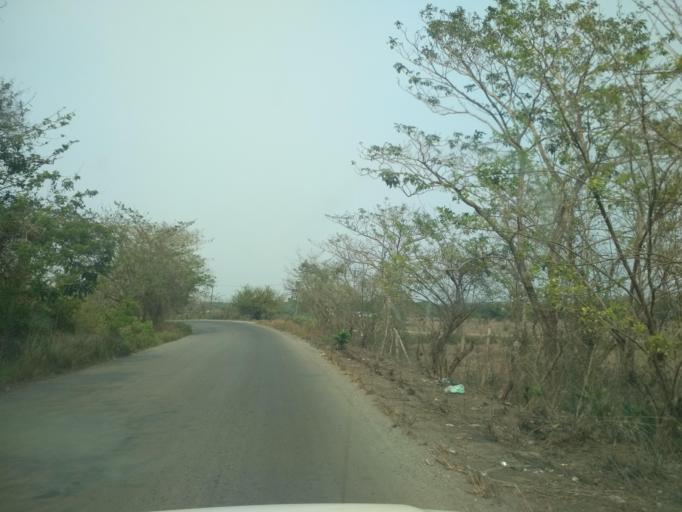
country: MX
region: Veracruz
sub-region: Veracruz
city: Delfino Victoria (Santa Fe)
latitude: 19.1889
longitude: -96.3012
